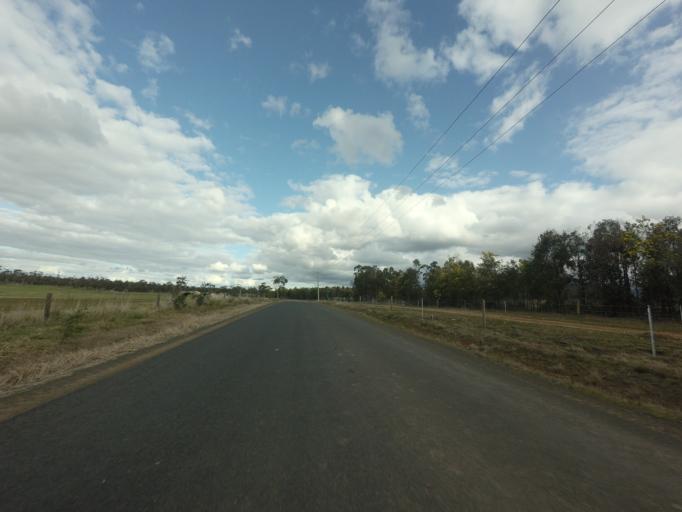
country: AU
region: Tasmania
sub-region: Northern Midlands
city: Longford
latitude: -41.8333
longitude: 147.2075
